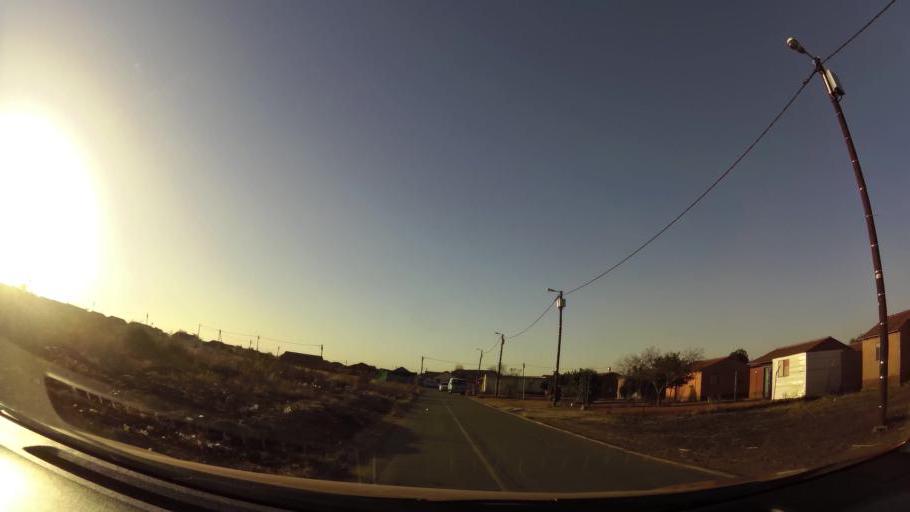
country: ZA
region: Gauteng
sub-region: City of Tshwane Metropolitan Municipality
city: Mabopane
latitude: -25.6014
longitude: 28.1096
